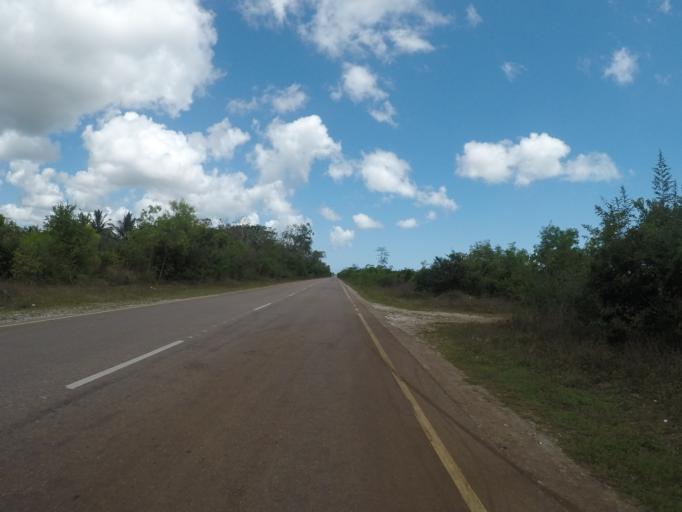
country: TZ
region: Zanzibar Central/South
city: Koani
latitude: -6.2545
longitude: 39.3566
